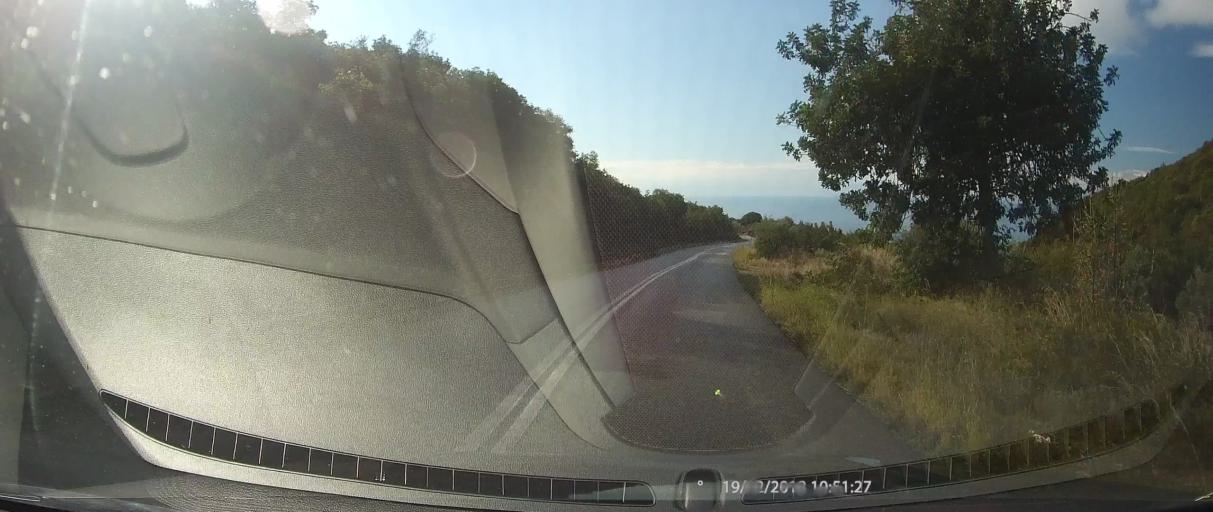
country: GR
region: Peloponnese
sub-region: Nomos Messinias
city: Kardamyli
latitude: 36.9155
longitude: 22.2158
